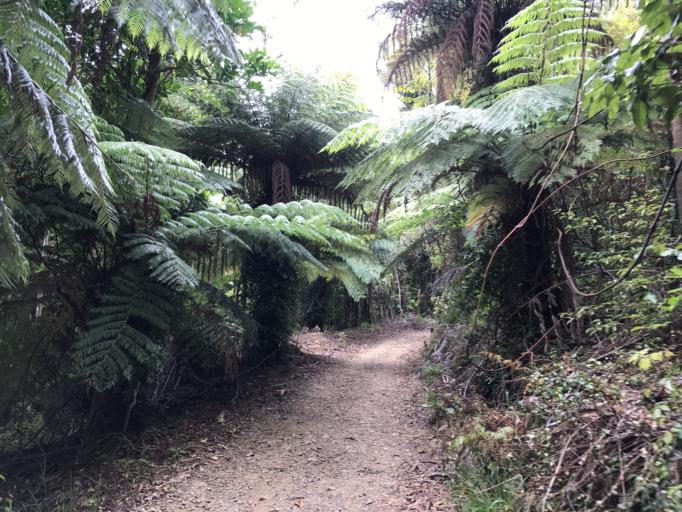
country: NZ
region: Marlborough
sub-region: Marlborough District
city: Picton
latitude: -41.0981
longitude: 174.1869
